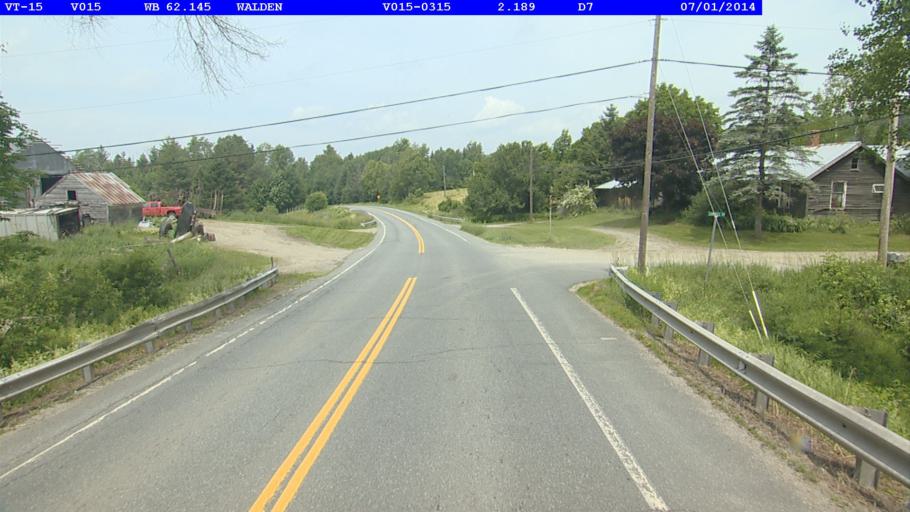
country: US
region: Vermont
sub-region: Caledonia County
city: Hardwick
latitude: 44.4668
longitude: -72.2710
